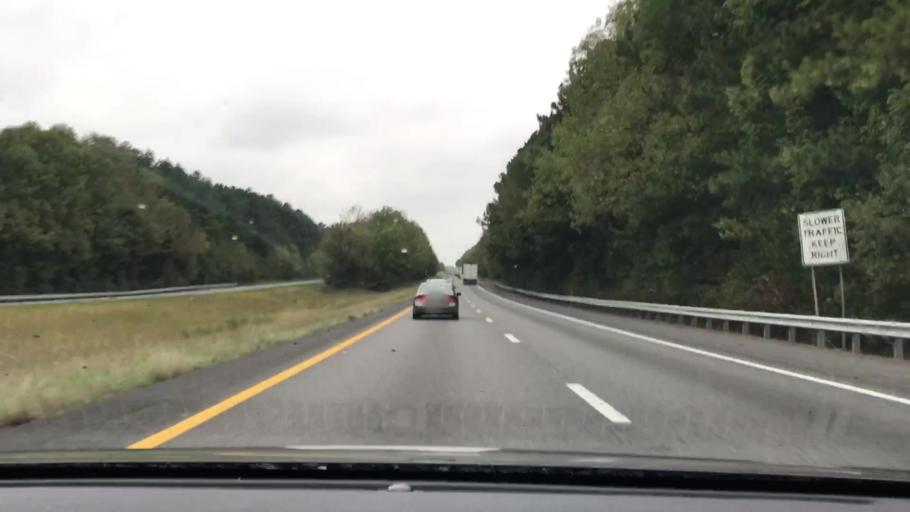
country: US
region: Tennessee
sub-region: Robertson County
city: Cross Plains
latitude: 36.5639
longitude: -86.6232
